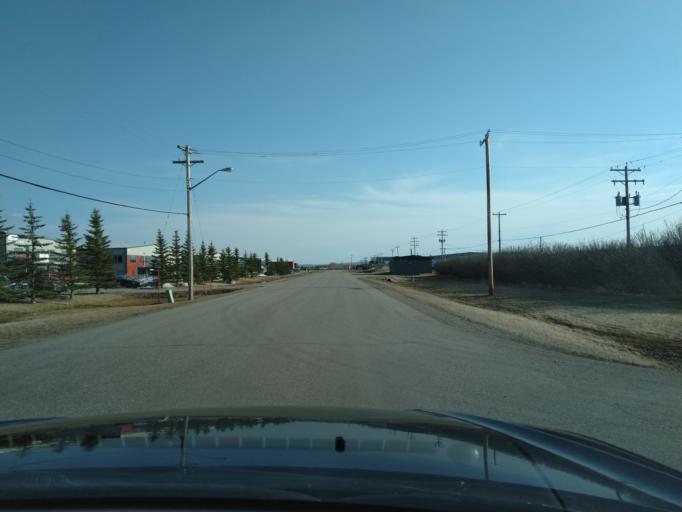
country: CA
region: Alberta
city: Cochrane
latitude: 51.1015
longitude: -114.3738
